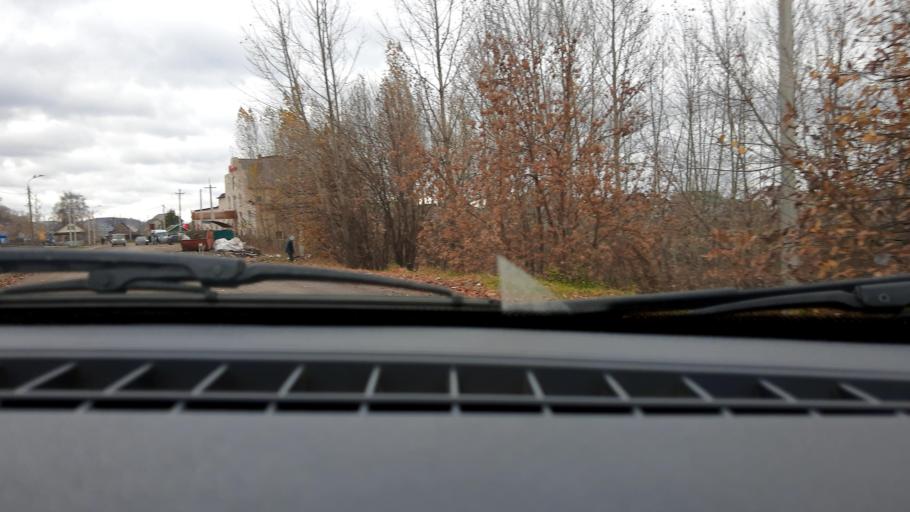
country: RU
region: Bashkortostan
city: Mikhaylovka
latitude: 54.7663
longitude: 55.9117
